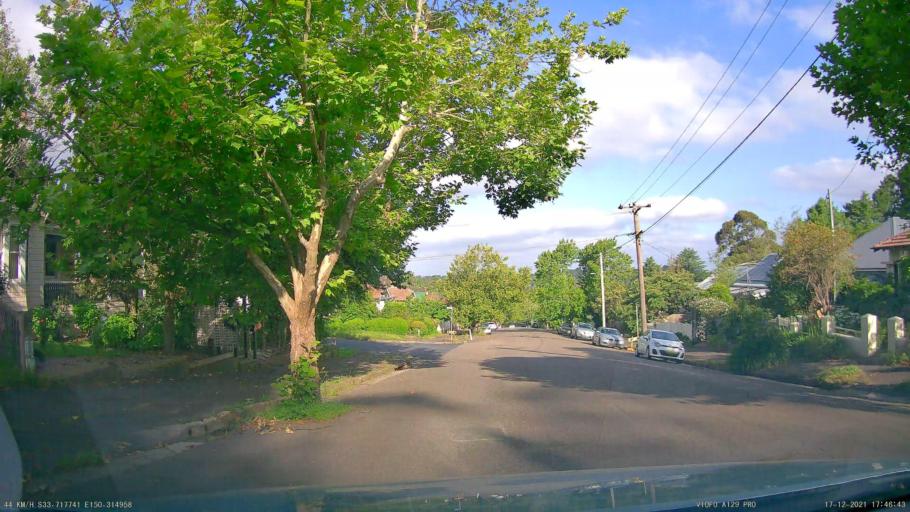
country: AU
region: New South Wales
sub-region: Blue Mountains Municipality
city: Katoomba
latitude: -33.7179
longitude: 150.3152
